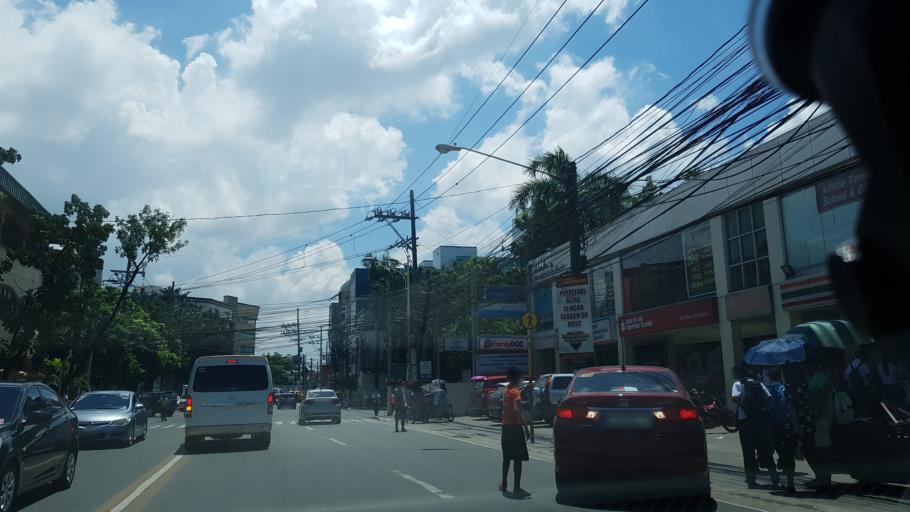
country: PH
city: Sambayanihan People's Village
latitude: 14.4568
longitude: 120.9946
